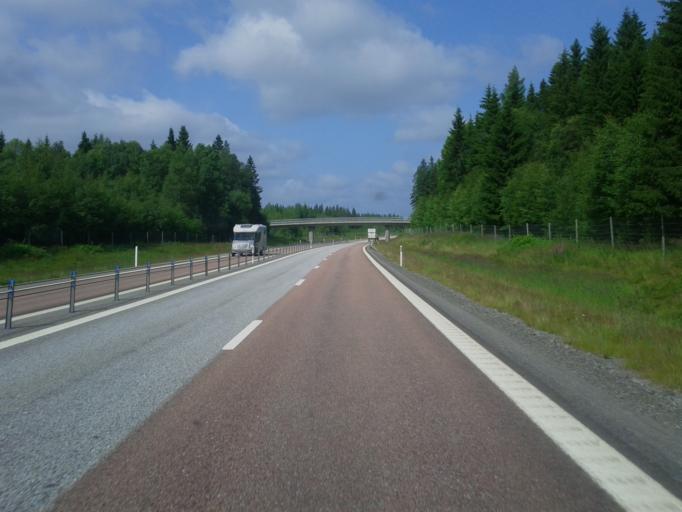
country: SE
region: Vaesterbotten
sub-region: Skelleftea Kommun
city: Soedra Bergsbyn
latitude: 64.6956
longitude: 21.0183
